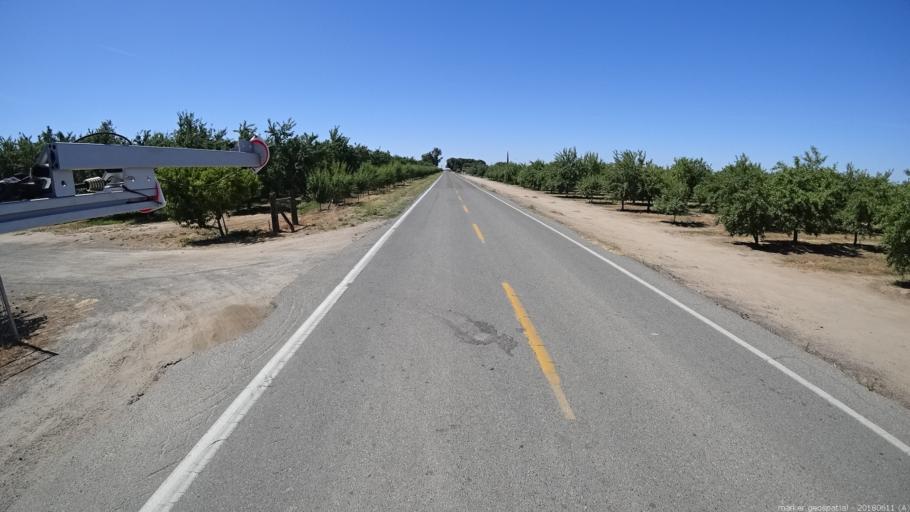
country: US
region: California
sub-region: Madera County
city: Fairmead
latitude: 37.0144
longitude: -120.2024
